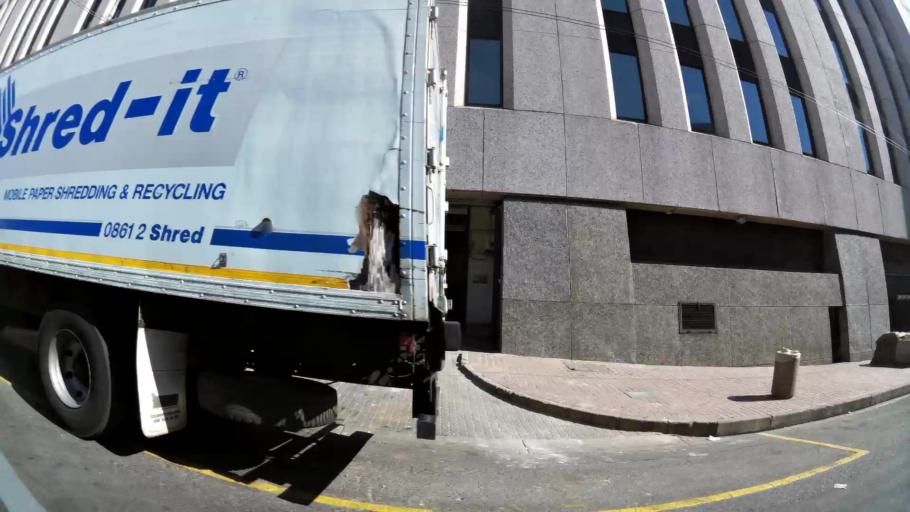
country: ZA
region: Gauteng
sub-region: City of Johannesburg Metropolitan Municipality
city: Johannesburg
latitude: -26.2097
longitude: 28.0409
